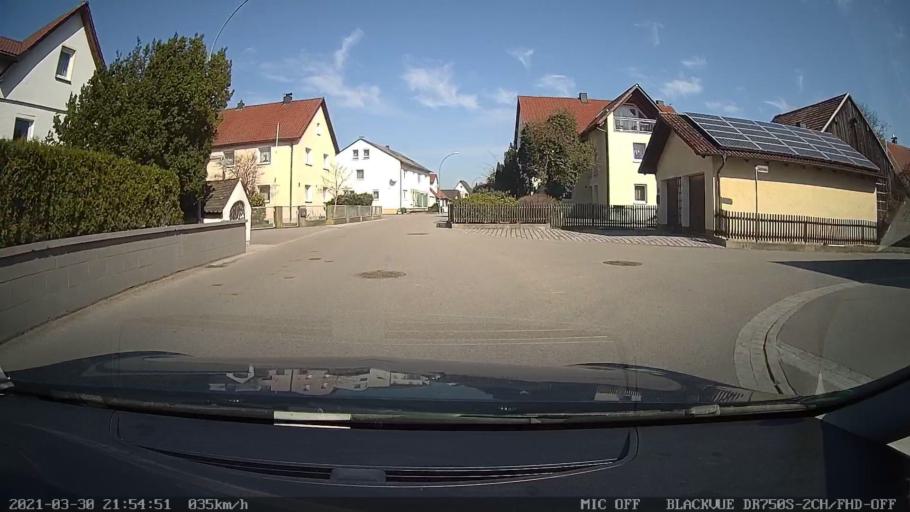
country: DE
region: Bavaria
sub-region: Upper Palatinate
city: Zeitlarn
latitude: 49.0971
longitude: 12.1120
